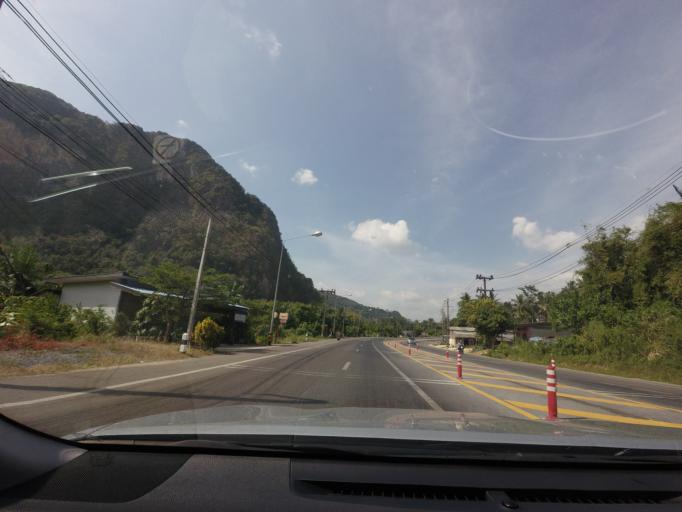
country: TH
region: Phangnga
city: Ban Ao Nang
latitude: 8.0809
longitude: 98.8041
